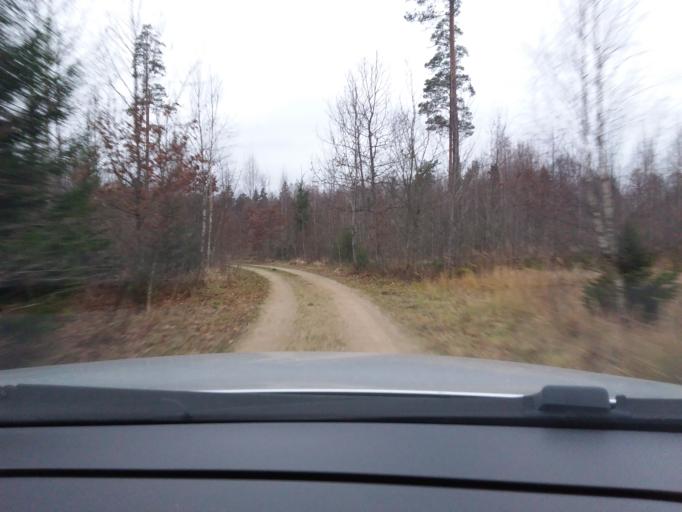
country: LV
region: Alsunga
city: Alsunga
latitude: 56.9555
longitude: 21.5394
